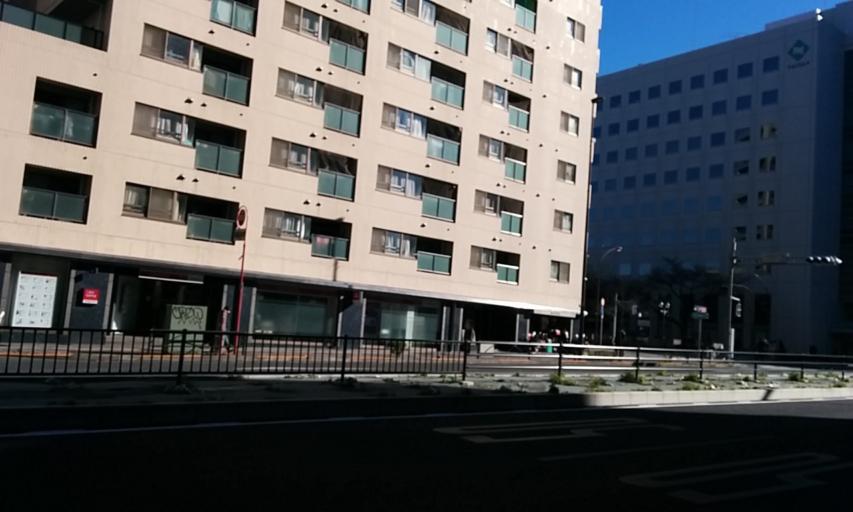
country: JP
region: Tokyo
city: Tokyo
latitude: 35.7158
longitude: 139.7394
